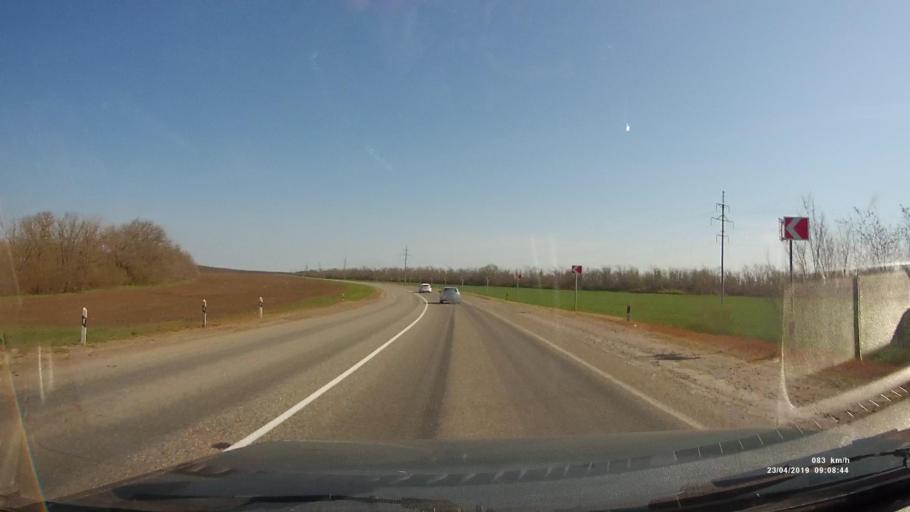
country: RU
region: Rostov
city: Sal'sk
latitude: 46.5651
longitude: 41.6111
